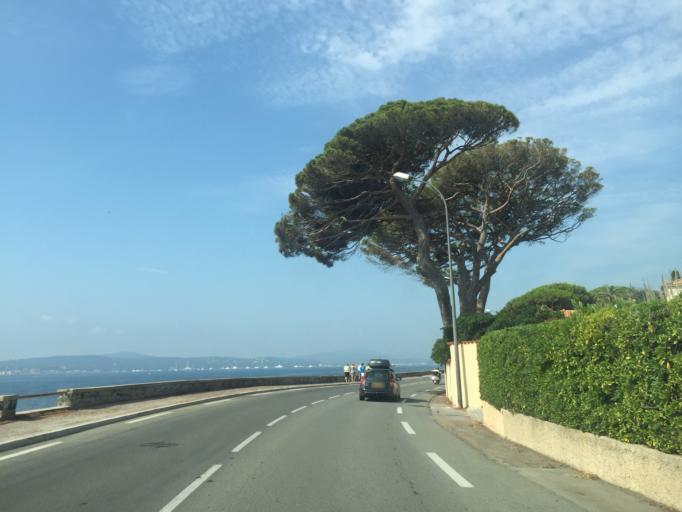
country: FR
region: Provence-Alpes-Cote d'Azur
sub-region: Departement du Var
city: Sainte-Maxime
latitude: 43.3087
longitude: 6.6495
